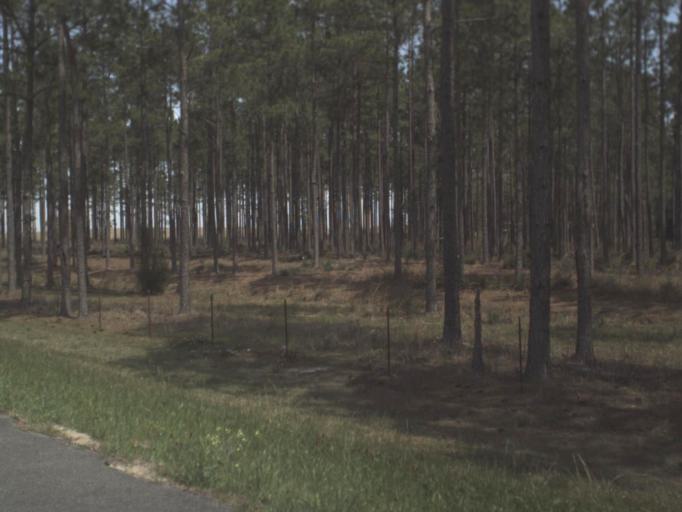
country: US
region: Florida
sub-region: Walton County
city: DeFuniak Springs
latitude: 30.8035
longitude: -85.9584
